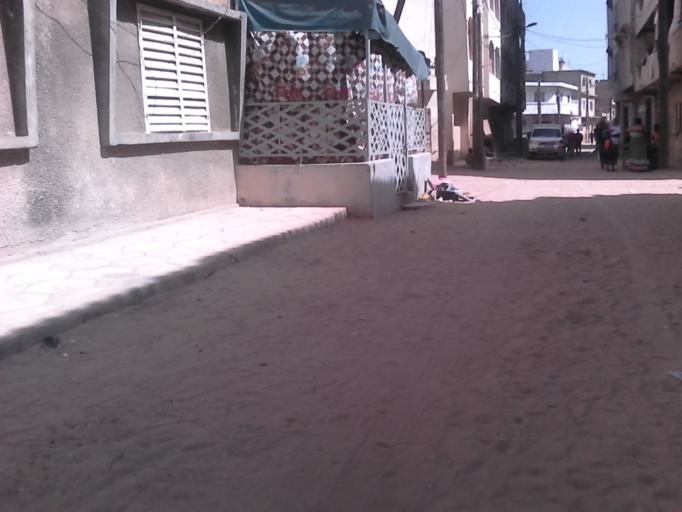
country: SN
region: Dakar
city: Grand Dakar
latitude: 14.7075
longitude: -17.4572
